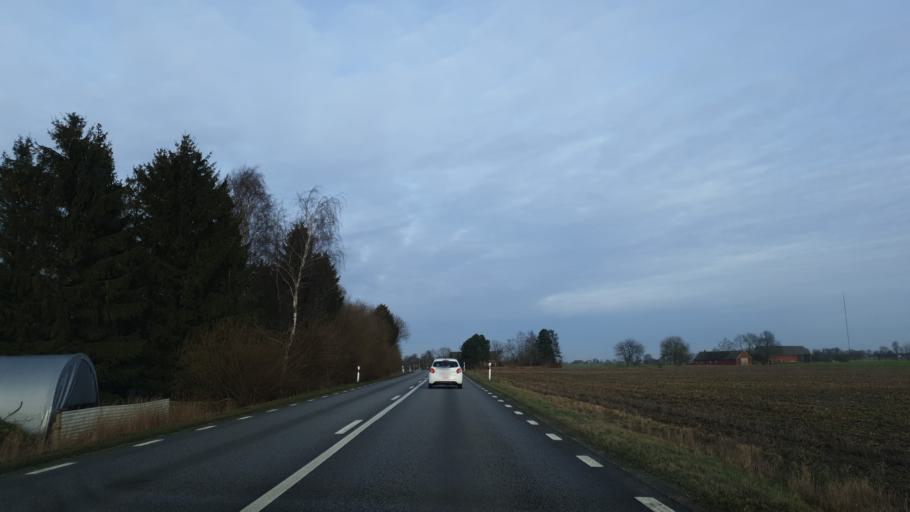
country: SE
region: Skane
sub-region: Horby Kommun
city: Hoerby
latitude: 55.7812
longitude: 13.6762
